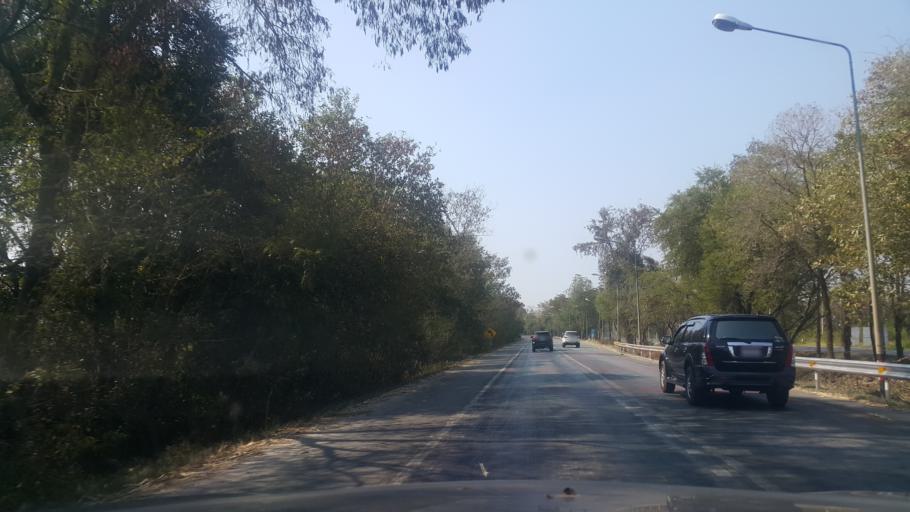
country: TH
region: Nakhon Ratchasima
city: Pak Thong Chai
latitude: 14.7330
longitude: 102.0217
